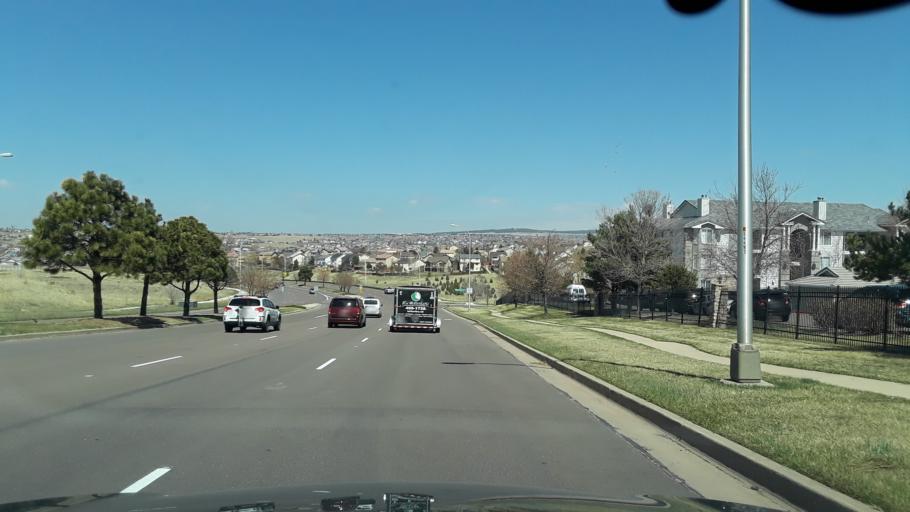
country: US
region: Colorado
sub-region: El Paso County
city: Cimarron Hills
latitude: 38.9239
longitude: -104.7383
